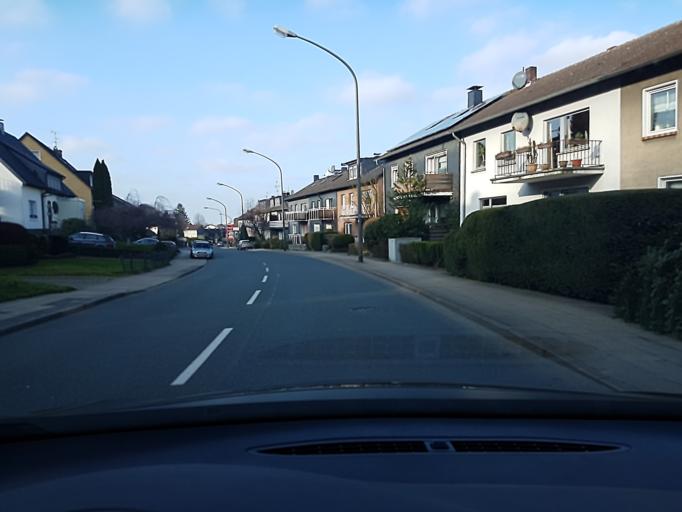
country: DE
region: North Rhine-Westphalia
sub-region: Regierungsbezirk Dusseldorf
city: Essen
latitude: 51.4204
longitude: 7.0941
